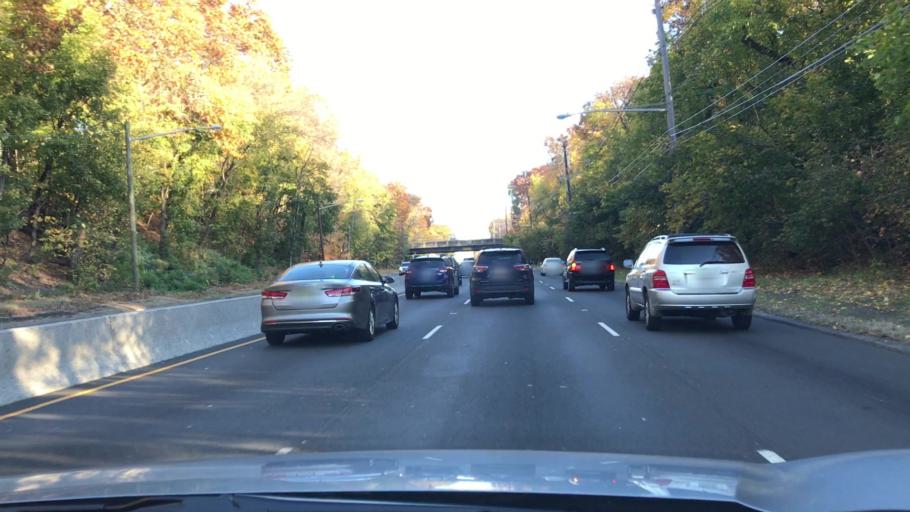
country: US
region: New Jersey
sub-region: Bergen County
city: Teaneck
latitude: 40.8965
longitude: -74.0207
